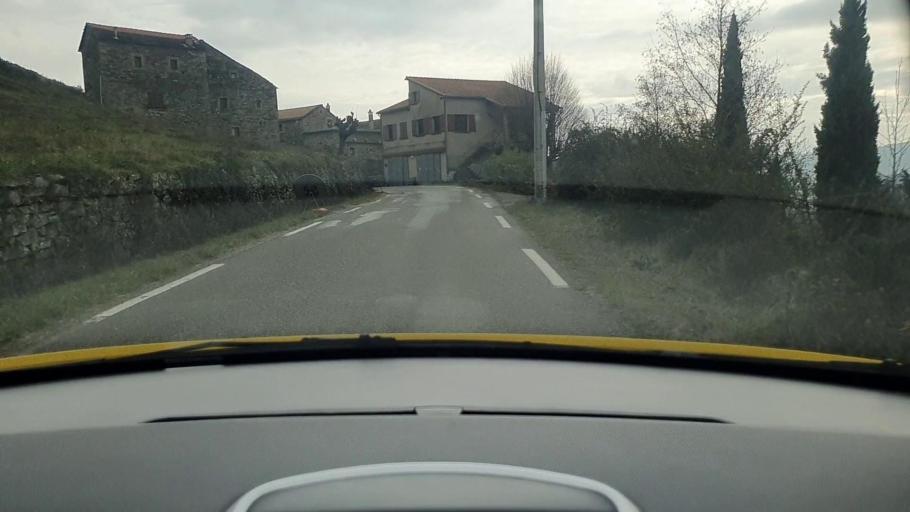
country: FR
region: Languedoc-Roussillon
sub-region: Departement du Gard
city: Besseges
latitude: 44.3392
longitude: 4.0470
